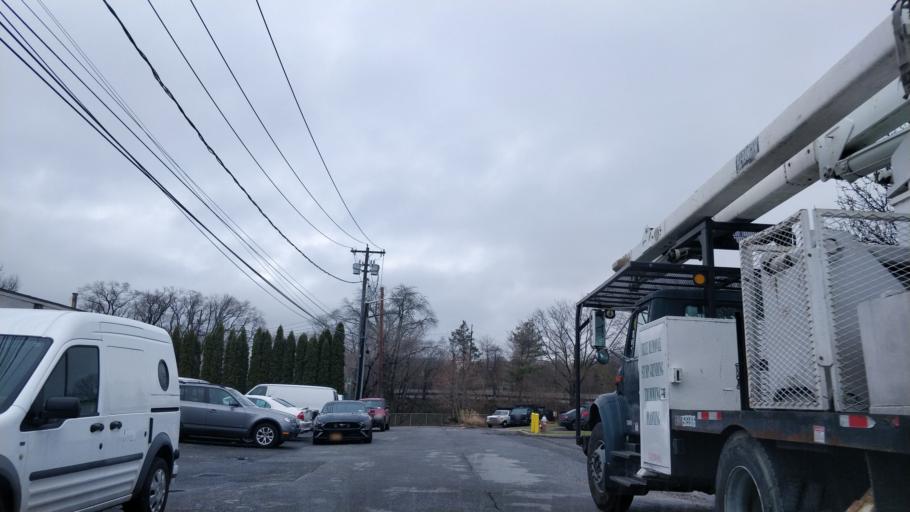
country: US
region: New York
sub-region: Nassau County
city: Glen Cove
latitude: 40.8535
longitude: -73.6211
